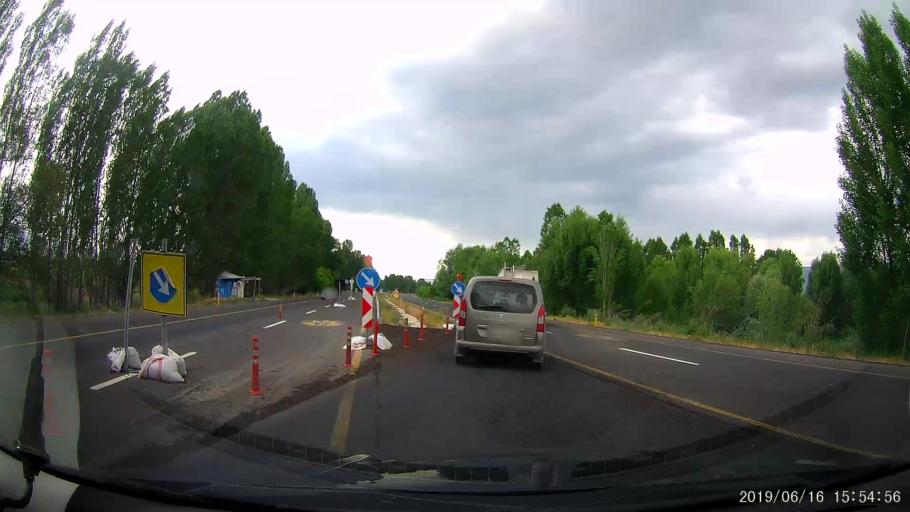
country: TR
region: Erzurum
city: Pasinler
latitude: 39.9777
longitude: 41.6281
